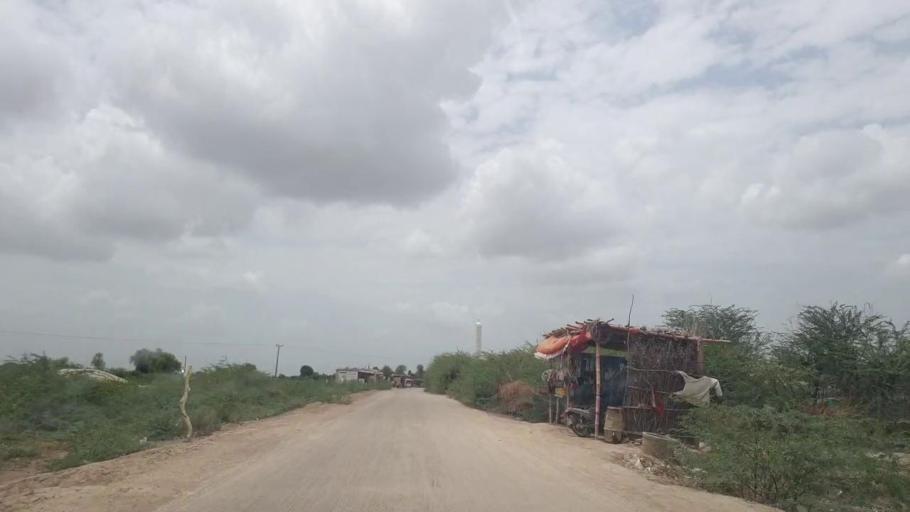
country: PK
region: Sindh
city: Naukot
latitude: 24.9166
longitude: 69.2718
